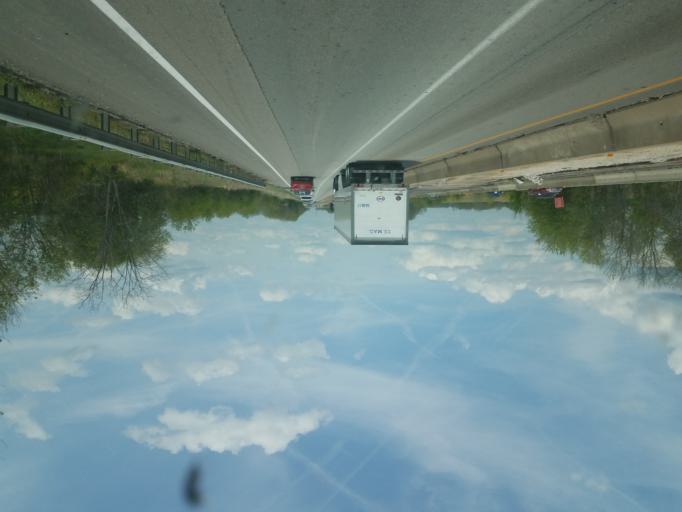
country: US
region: Kentucky
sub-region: Hardin County
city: Elizabethtown
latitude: 37.5607
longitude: -85.8762
